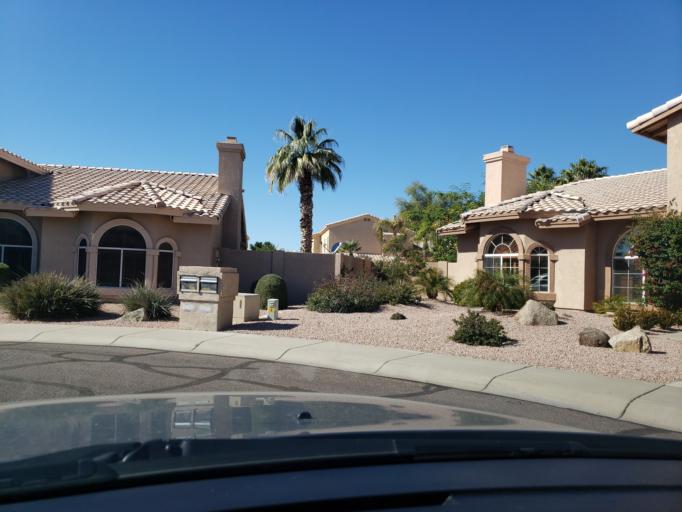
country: US
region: Arizona
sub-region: Maricopa County
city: Paradise Valley
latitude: 33.6152
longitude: -111.9284
